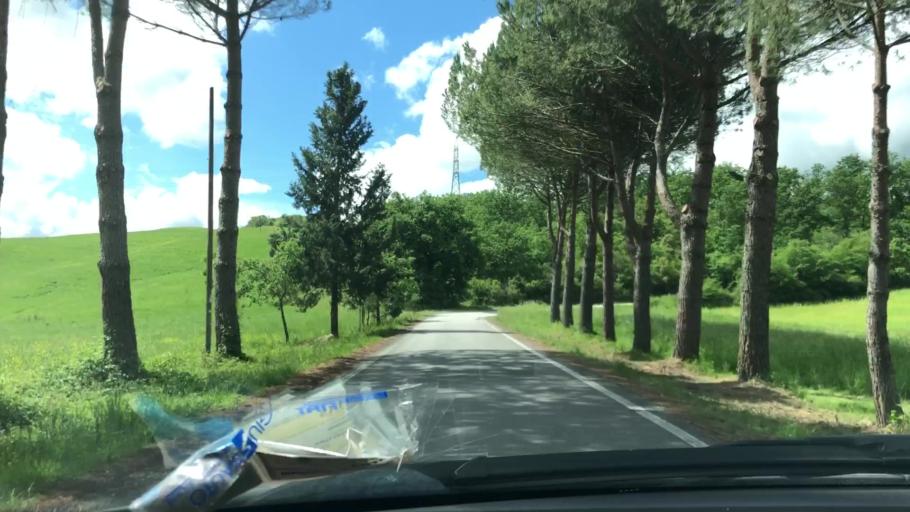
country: IT
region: Tuscany
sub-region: Province of Pisa
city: Saline
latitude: 43.3478
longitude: 10.7922
